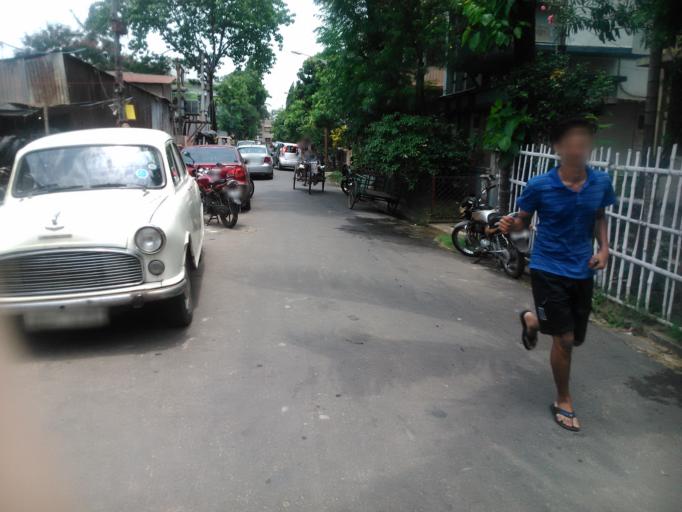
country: IN
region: West Bengal
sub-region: North 24 Parganas
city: Garui
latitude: 22.5946
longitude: 88.4088
